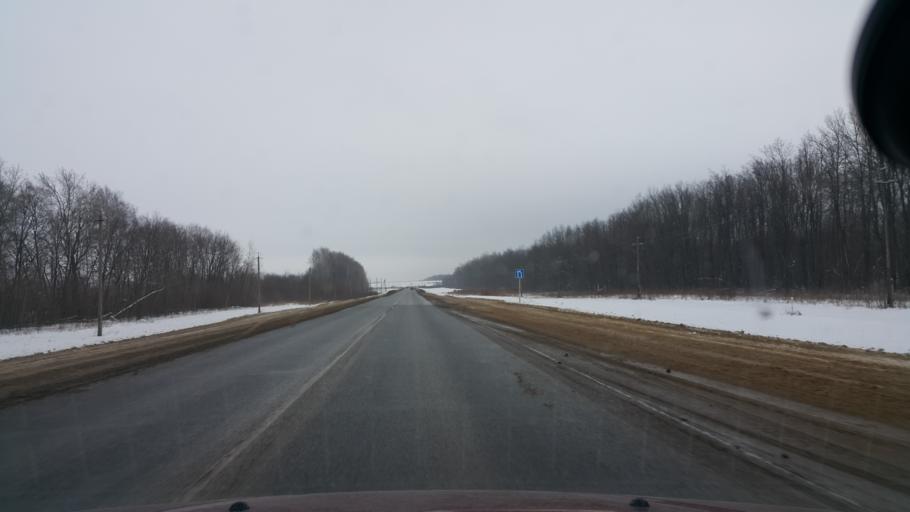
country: RU
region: Tambov
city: Kotovsk
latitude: 52.5854
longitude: 41.4495
